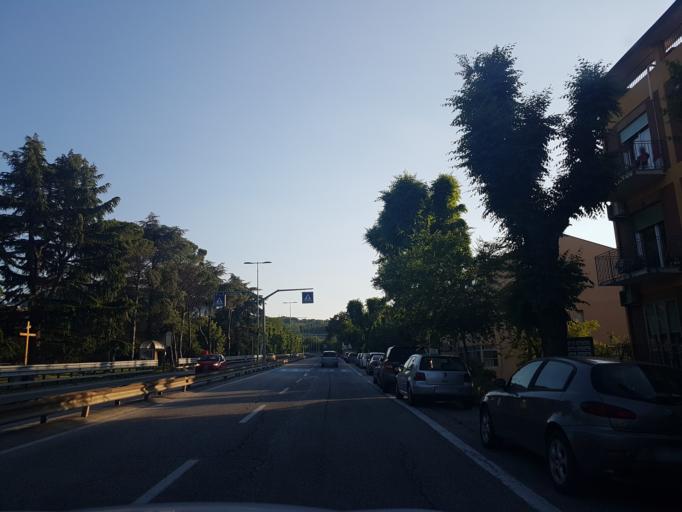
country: SM
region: Serravalle
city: Serravalle
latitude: 43.9668
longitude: 12.4743
